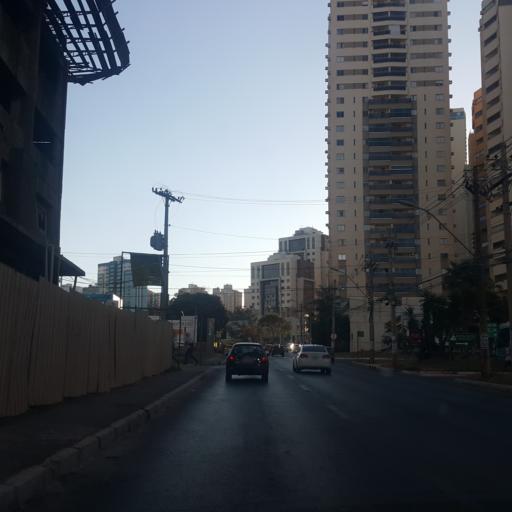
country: BR
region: Federal District
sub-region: Brasilia
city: Brasilia
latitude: -15.8384
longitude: -48.0296
